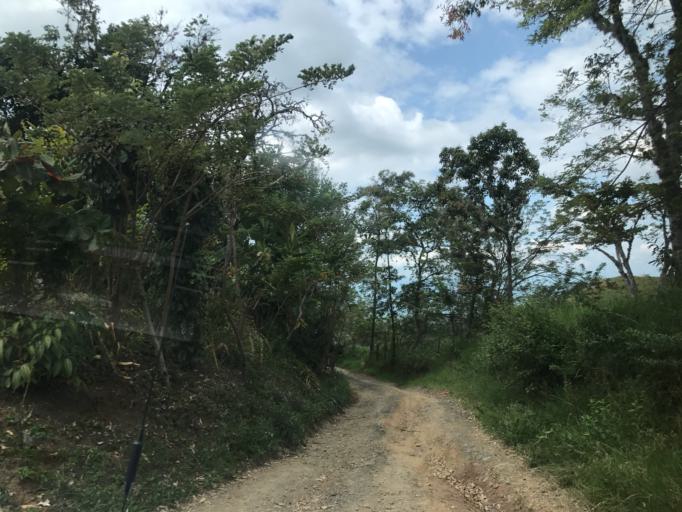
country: CO
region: Valle del Cauca
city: Obando
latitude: 4.5562
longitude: -75.9244
